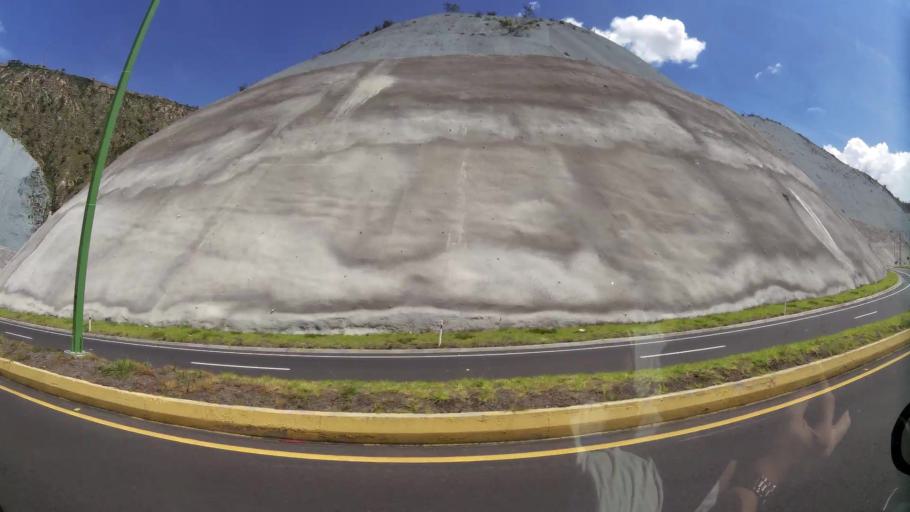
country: EC
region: Pichincha
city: Quito
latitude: -0.0993
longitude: -78.3886
